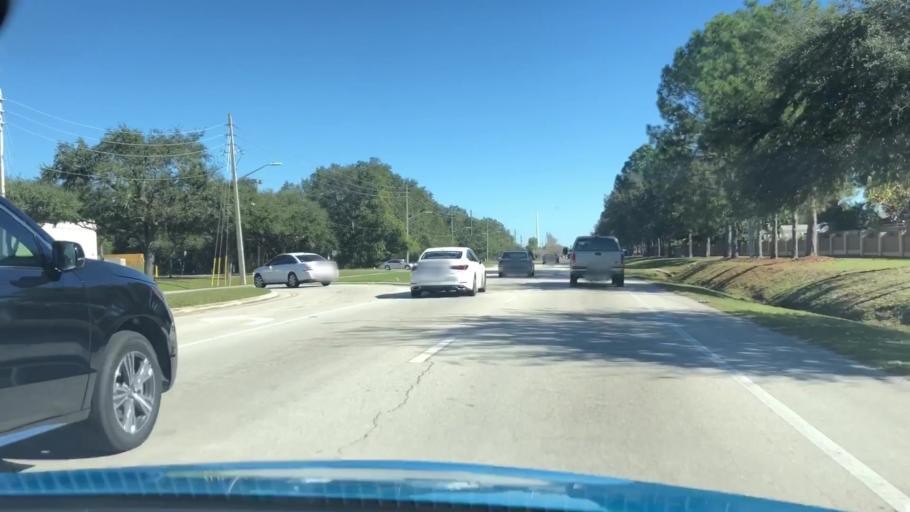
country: US
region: Florida
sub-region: Orange County
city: Oak Ridge
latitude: 28.4869
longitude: -81.4158
